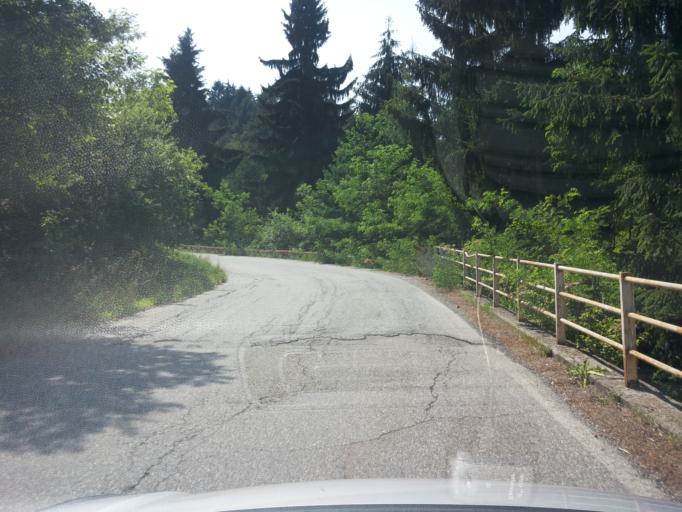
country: IT
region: Piedmont
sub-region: Provincia di Biella
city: Lanvario
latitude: 45.6537
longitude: 8.1957
